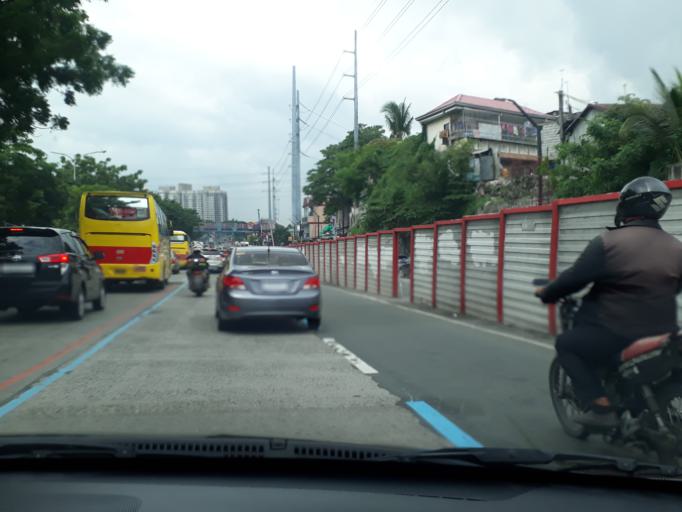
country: PH
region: Calabarzon
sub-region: Province of Rizal
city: Pateros
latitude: 14.5372
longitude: 121.0574
